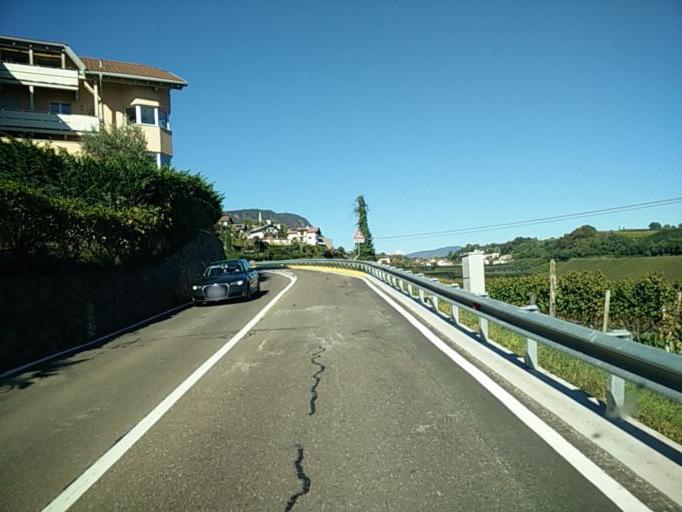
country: IT
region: Trentino-Alto Adige
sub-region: Bolzano
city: Caldaro sulla Strada del Vino
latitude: 46.4054
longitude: 11.2485
